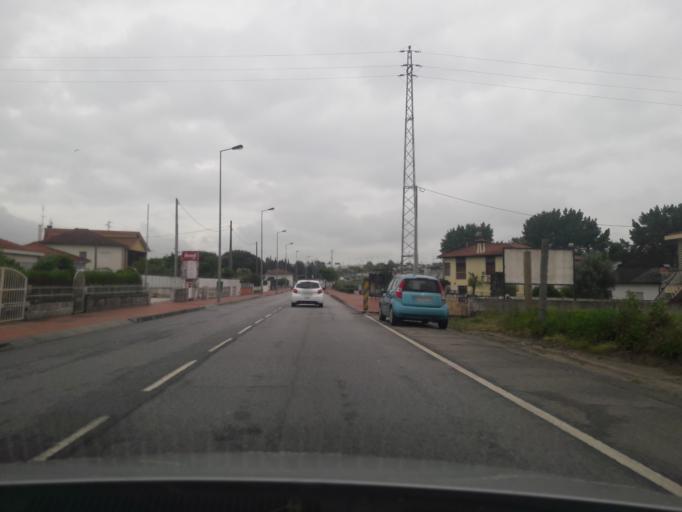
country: PT
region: Porto
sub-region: Vila do Conde
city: Arvore
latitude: 41.3366
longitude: -8.7251
